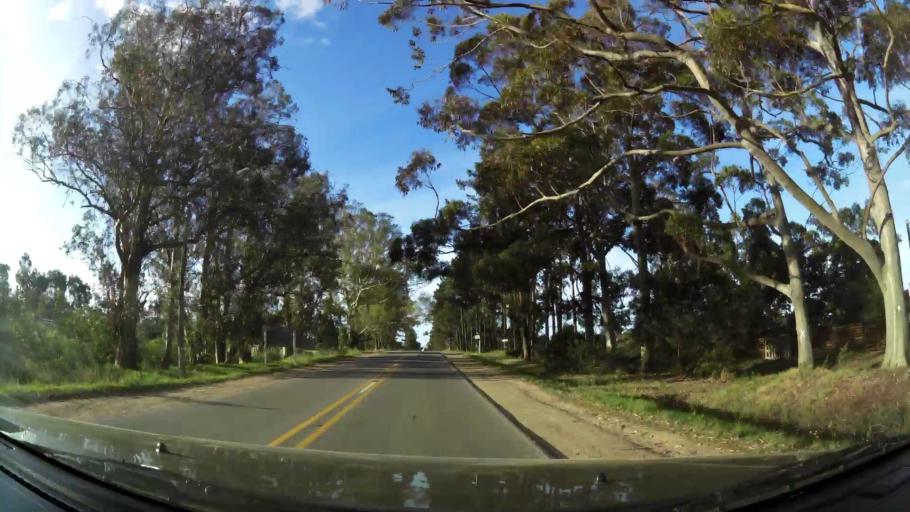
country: UY
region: Canelones
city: Atlantida
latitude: -34.7661
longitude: -55.8425
